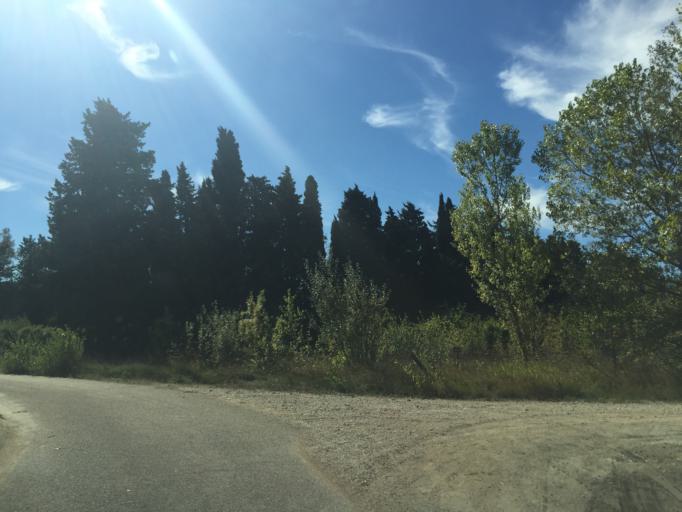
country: FR
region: Provence-Alpes-Cote d'Azur
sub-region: Departement du Vaucluse
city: Piolenc
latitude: 44.1503
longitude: 4.7509
